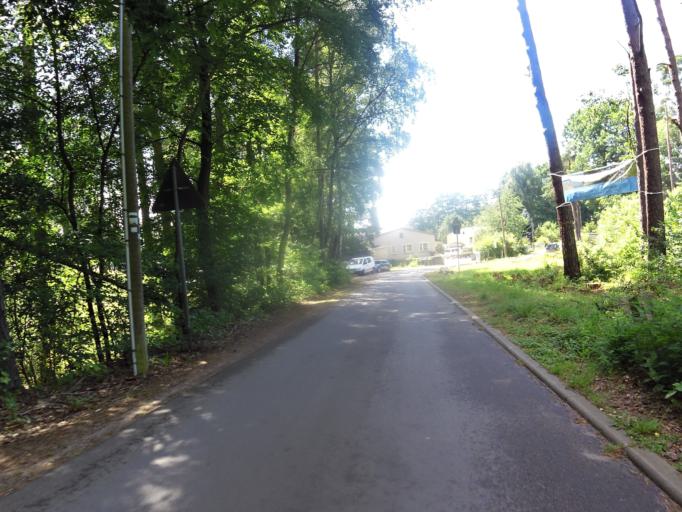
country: DE
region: Brandenburg
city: Lychen
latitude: 53.2077
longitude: 13.2773
